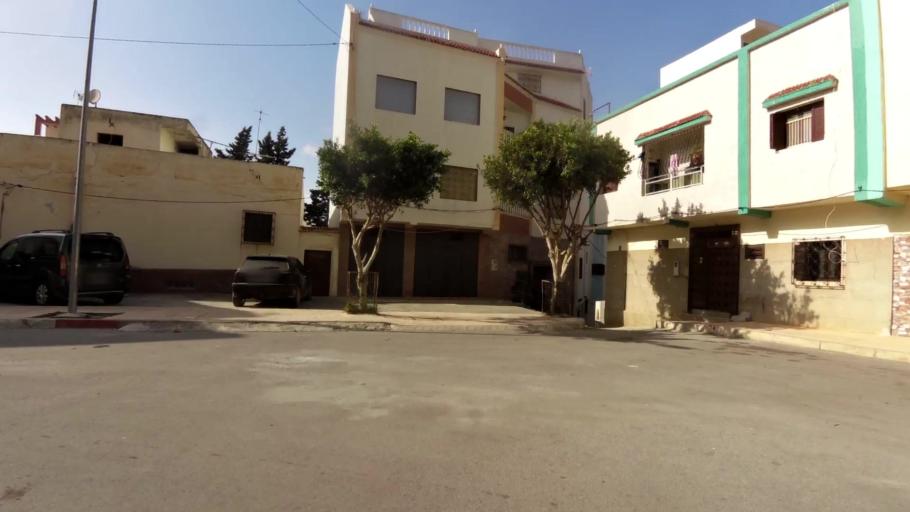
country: MA
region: Tanger-Tetouan
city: Tetouan
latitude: 35.5963
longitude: -5.3431
